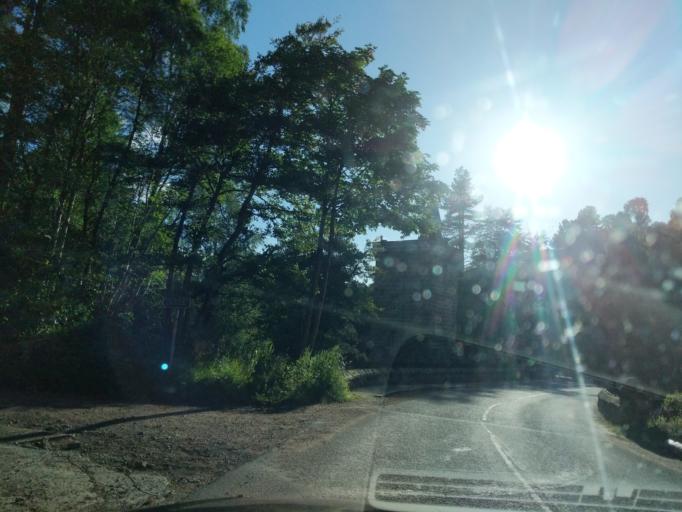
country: GB
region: Scotland
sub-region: Aberdeenshire
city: Aboyne
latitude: 57.0633
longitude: -2.8179
